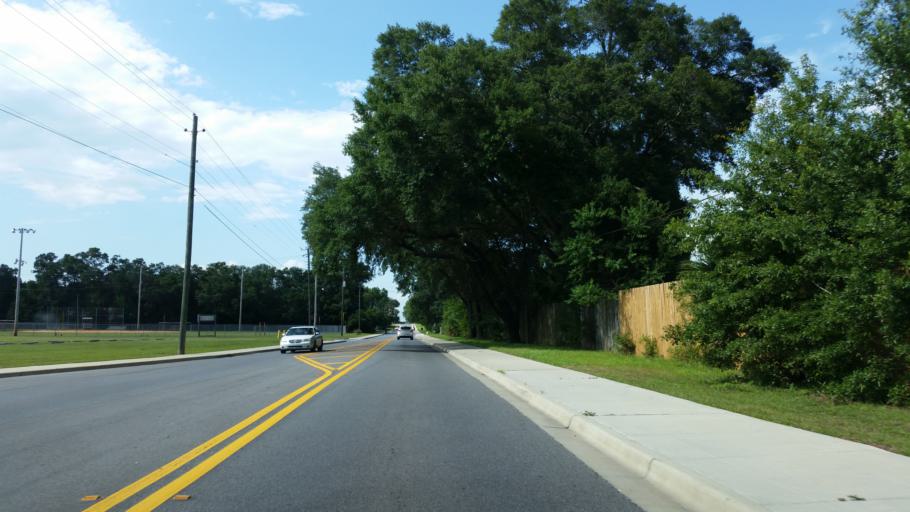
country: US
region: Florida
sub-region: Escambia County
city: Ensley
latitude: 30.5353
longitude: -87.2476
